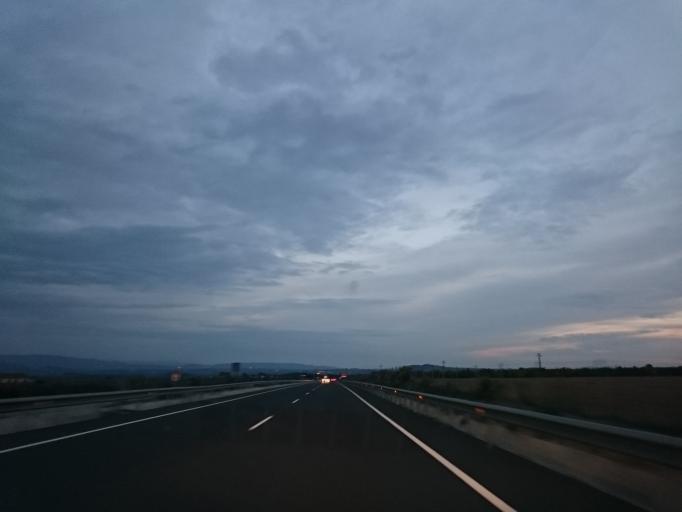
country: ES
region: Catalonia
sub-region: Provincia de Barcelona
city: Sant Pere de Riudebitlles
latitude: 41.4250
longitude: 1.6841
